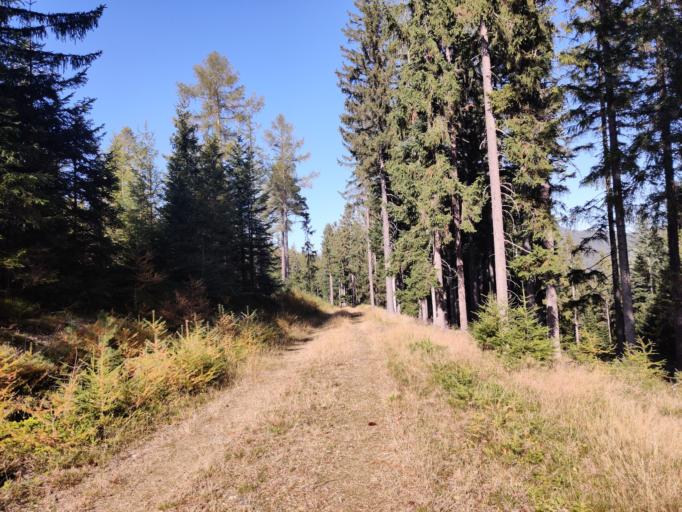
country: AT
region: Styria
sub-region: Politischer Bezirk Hartberg-Fuerstenfeld
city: Sankt Jakob im Walde
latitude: 47.4732
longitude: 15.8078
